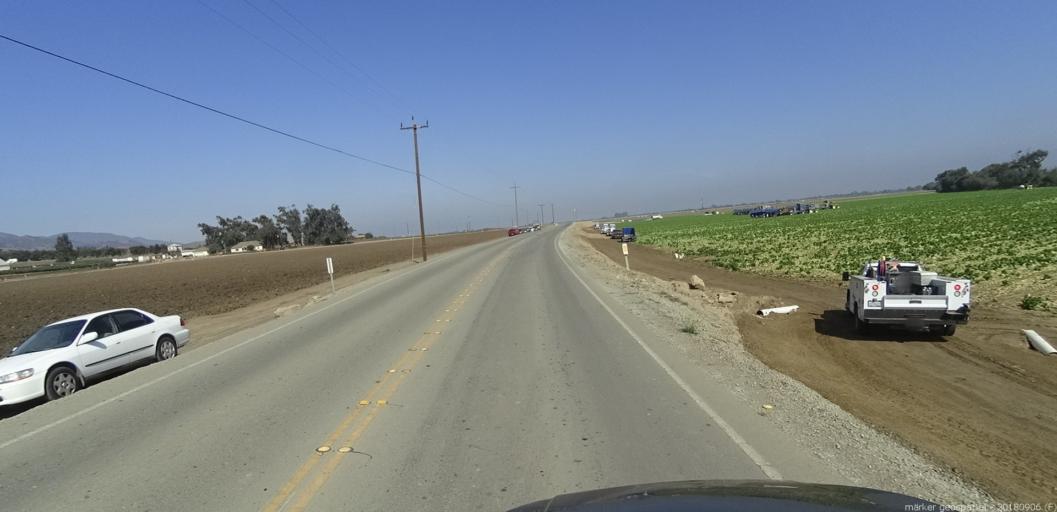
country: US
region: California
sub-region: Monterey County
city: Chualar
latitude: 36.5579
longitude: -121.5518
